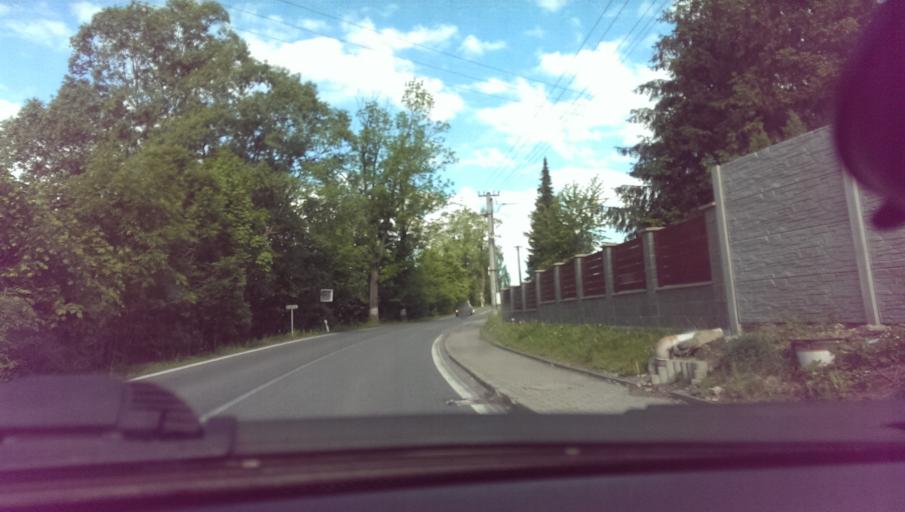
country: CZ
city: Kuncice pod Ondrejnikem
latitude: 49.5391
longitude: 18.2921
